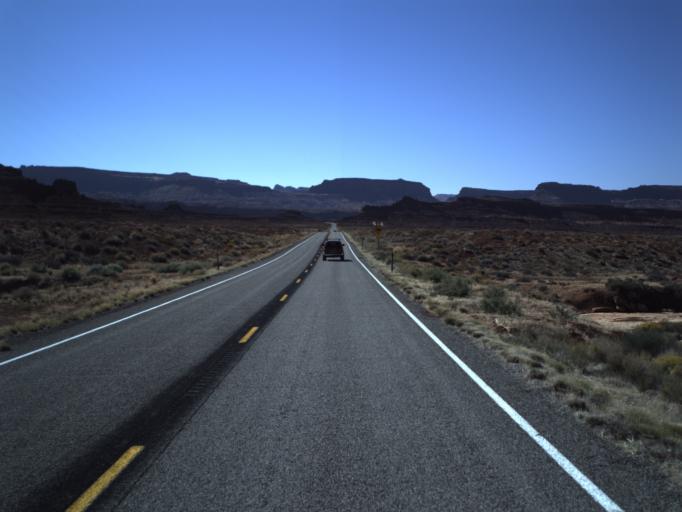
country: US
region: Utah
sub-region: San Juan County
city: Blanding
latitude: 37.8485
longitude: -110.3544
